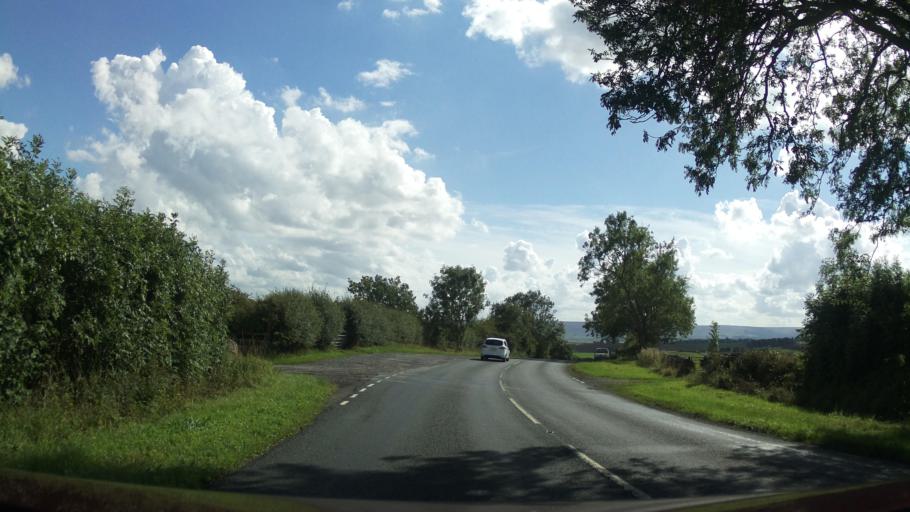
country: GB
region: England
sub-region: North Yorkshire
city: Leyburn
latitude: 54.3378
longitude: -1.8192
